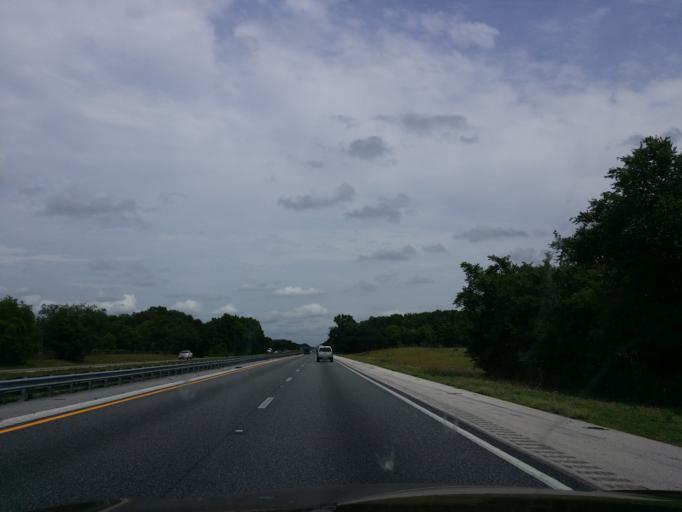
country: US
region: Florida
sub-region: Sumter County
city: Lake Panasoffkee
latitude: 28.7840
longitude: -82.0870
